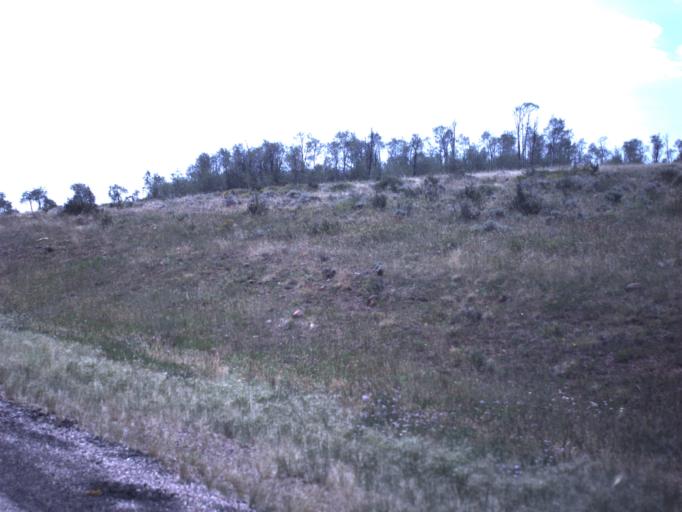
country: US
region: Utah
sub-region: Uintah County
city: Maeser
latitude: 40.6794
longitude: -109.4885
